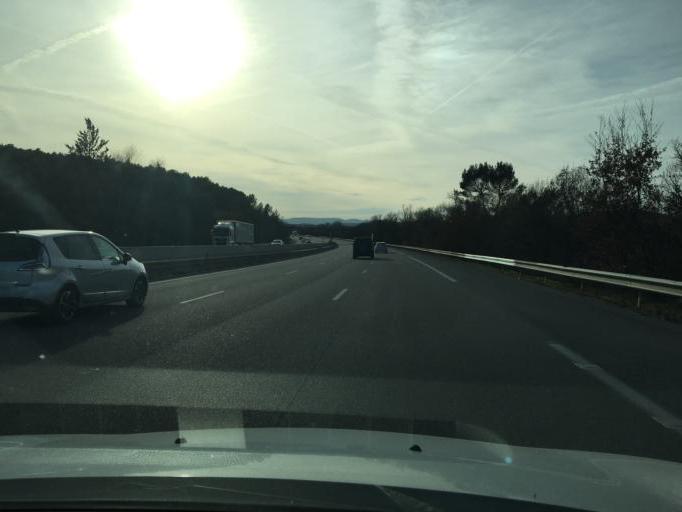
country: FR
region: Provence-Alpes-Cote d'Azur
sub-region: Departement du Var
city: Les Arcs
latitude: 43.4520
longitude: 6.5096
